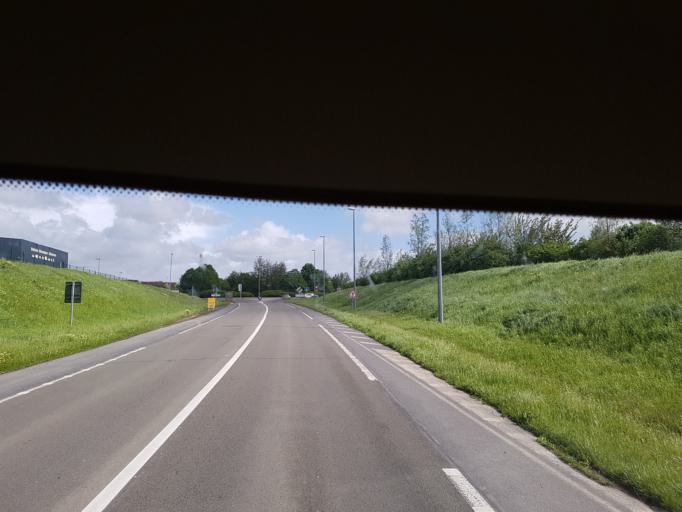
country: FR
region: Nord-Pas-de-Calais
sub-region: Departement du Nord
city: Proville
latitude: 50.1731
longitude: 3.1964
